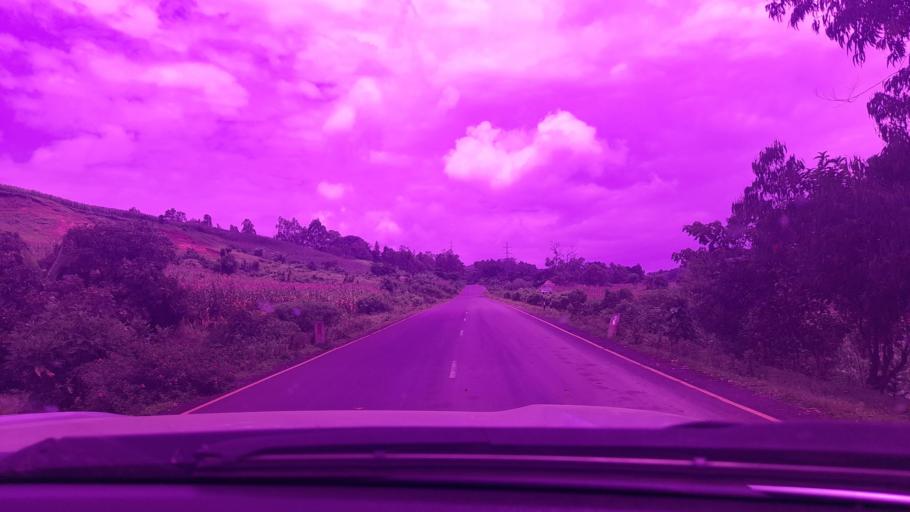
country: ET
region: Oromiya
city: Metu
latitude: 8.3276
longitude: 35.7578
